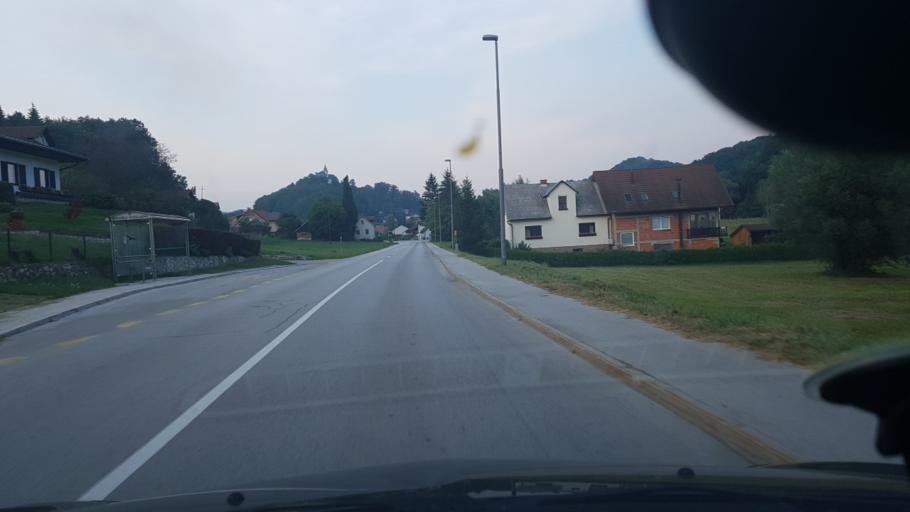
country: SI
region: Rogaska Slatina
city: Rogaska Slatina
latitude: 46.2268
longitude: 15.6465
